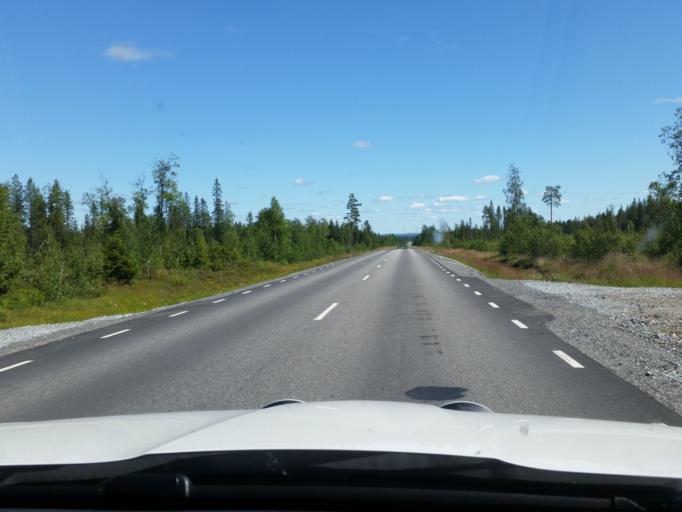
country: SE
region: Vaesterbotten
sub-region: Skelleftea Kommun
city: Storvik
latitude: 65.3238
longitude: 20.7794
